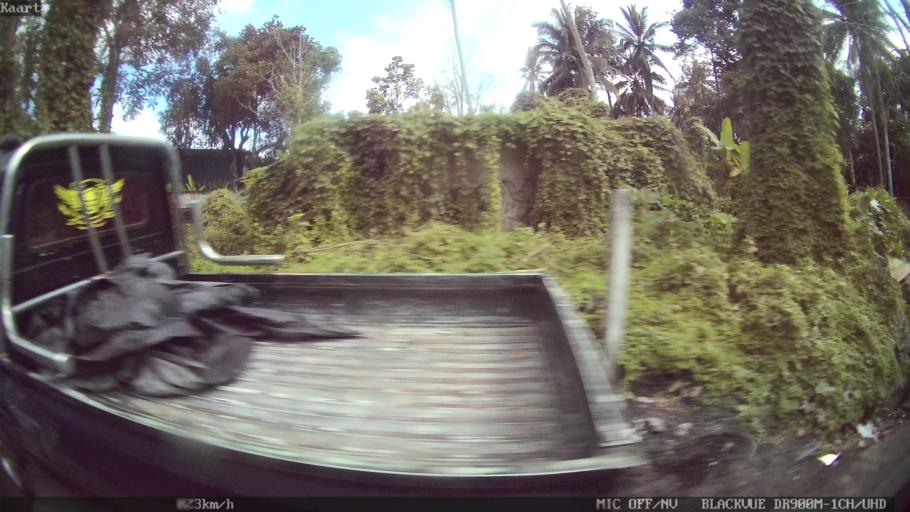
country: ID
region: Bali
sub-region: Kabupaten Gianyar
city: Ubud
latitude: -8.5094
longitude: 115.2758
